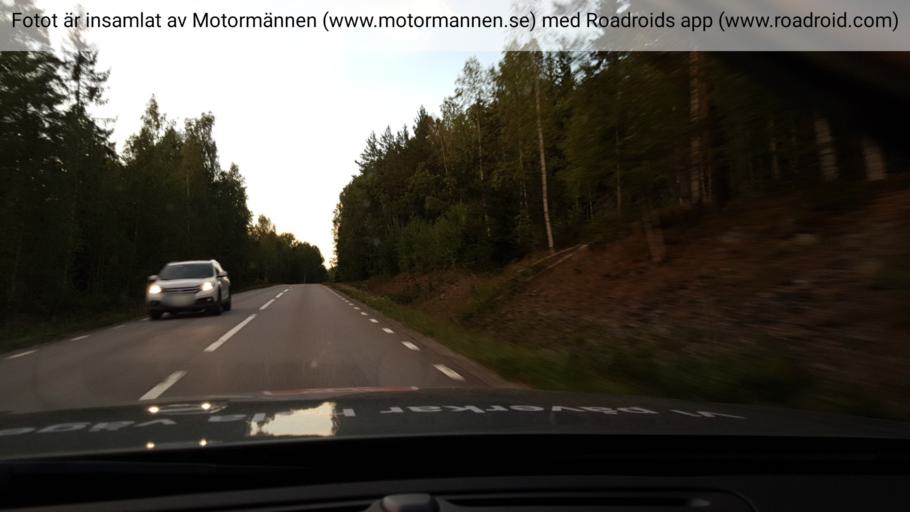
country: SE
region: OErebro
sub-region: Hallefors Kommun
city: Haellefors
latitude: 59.6854
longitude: 14.5251
